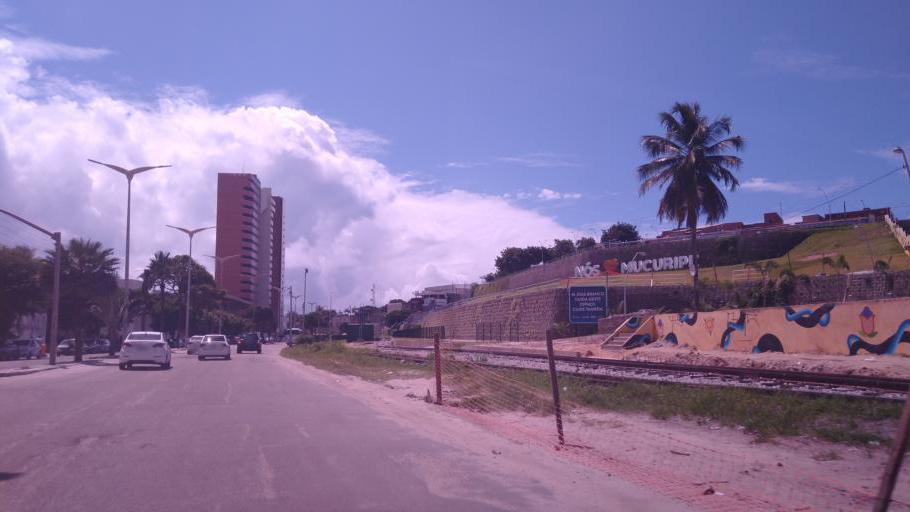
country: BR
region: Ceara
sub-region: Fortaleza
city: Fortaleza
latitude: -3.7216
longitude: -38.4786
